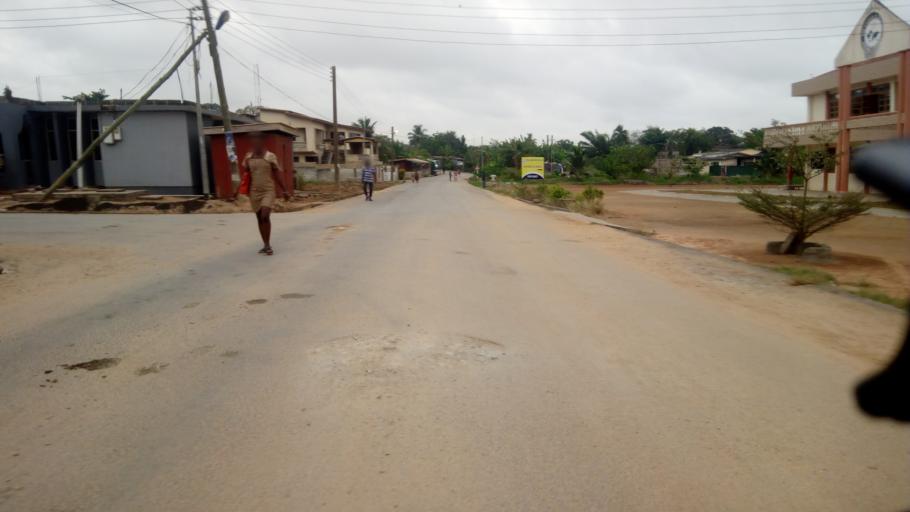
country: GH
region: Central
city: Cape Coast
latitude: 5.1188
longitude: -1.2694
